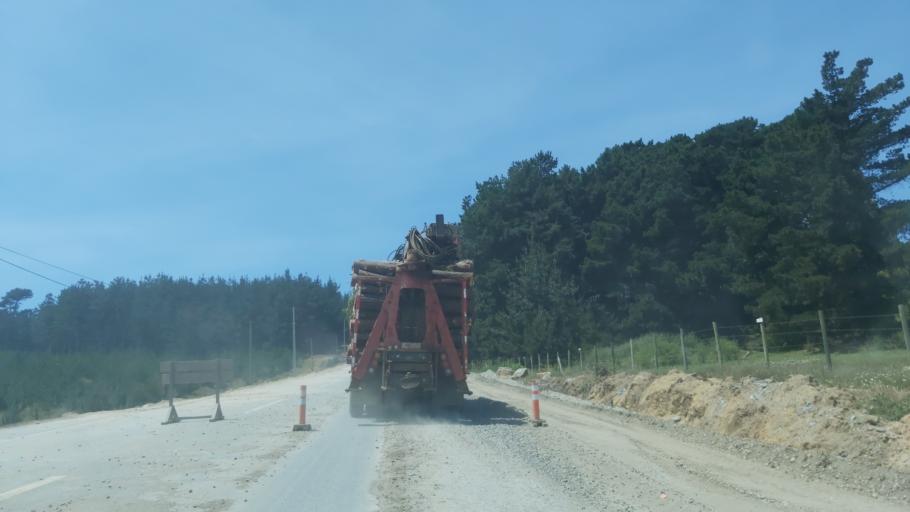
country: CL
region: Maule
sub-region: Provincia de Talca
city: Constitucion
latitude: -35.4504
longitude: -72.4782
